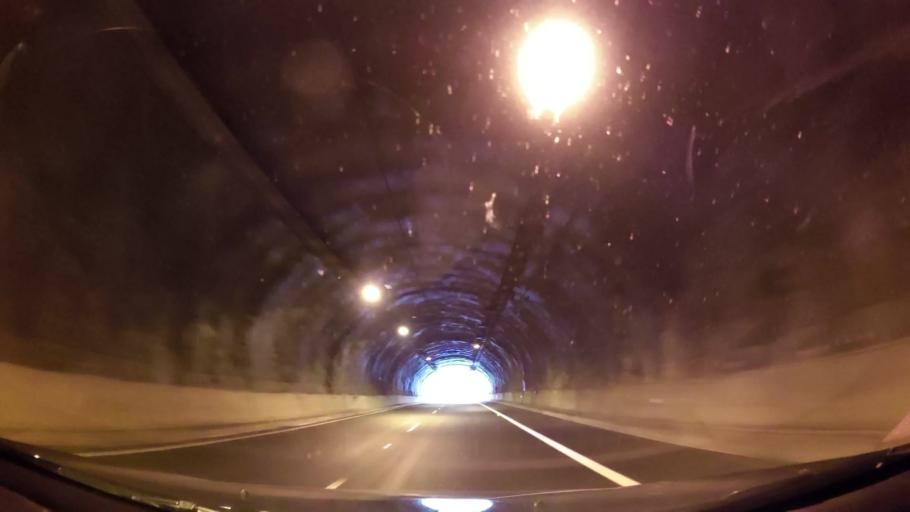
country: CL
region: Santiago Metropolitan
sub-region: Provincia de Santiago
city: Santiago
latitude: -33.3696
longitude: -70.6121
